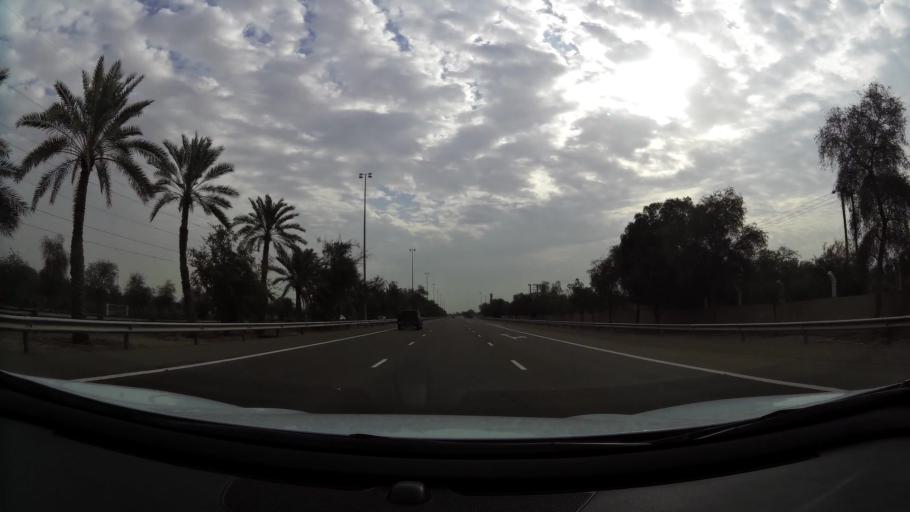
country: AE
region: Abu Dhabi
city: Al Ain
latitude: 24.2039
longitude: 55.4128
